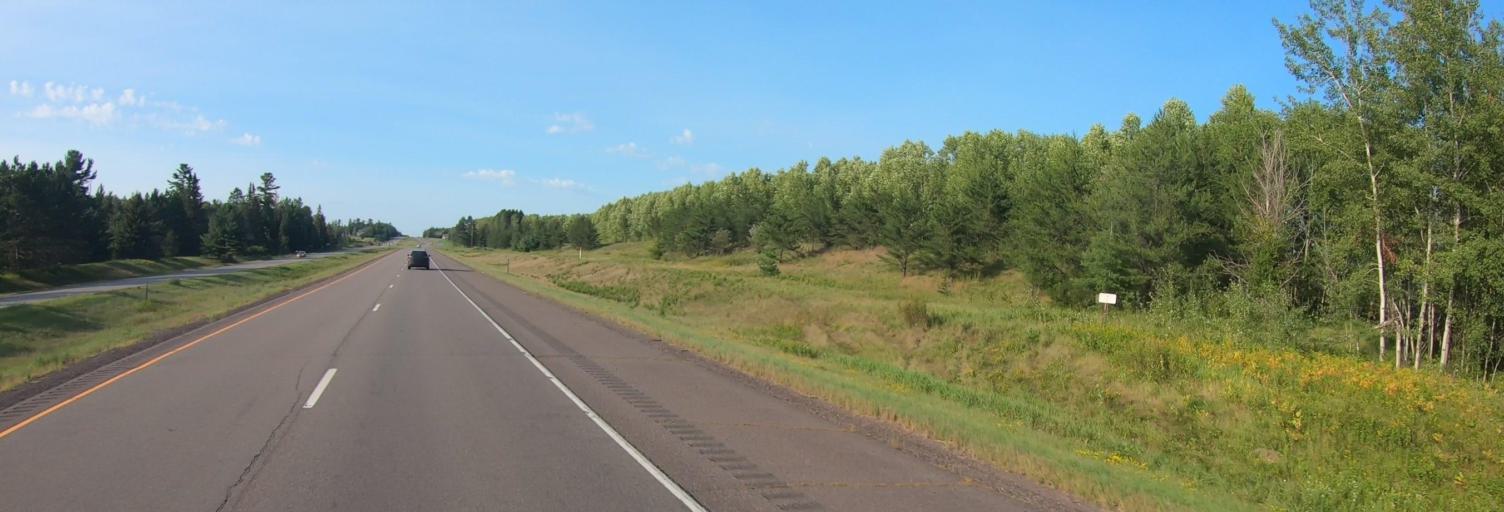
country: US
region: Minnesota
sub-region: Carlton County
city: Cloquet
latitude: 47.0215
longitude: -92.4705
